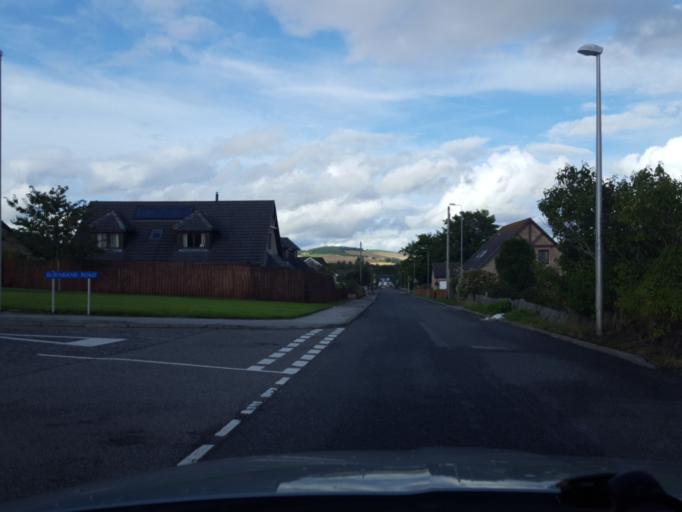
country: GB
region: Scotland
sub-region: Aberdeenshire
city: Alford
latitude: 57.2287
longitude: -2.7058
